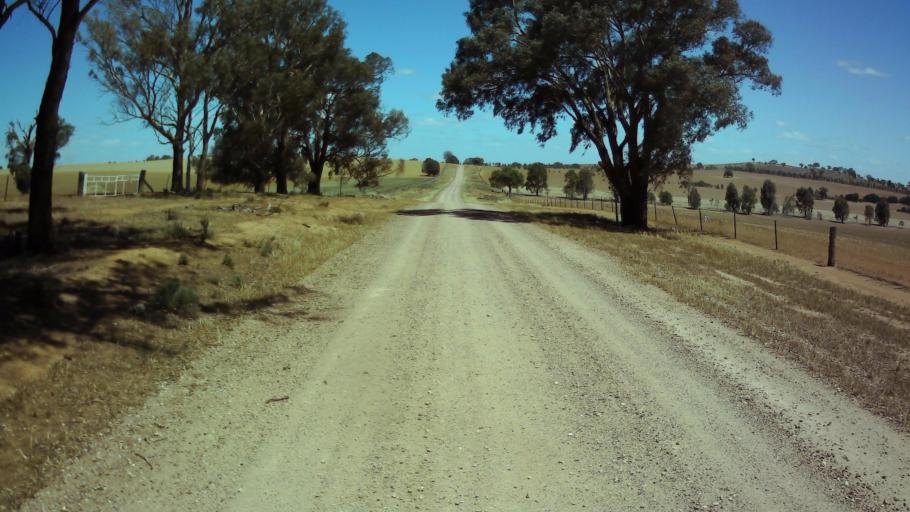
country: AU
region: New South Wales
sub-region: Weddin
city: Grenfell
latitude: -33.9422
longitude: 148.3298
